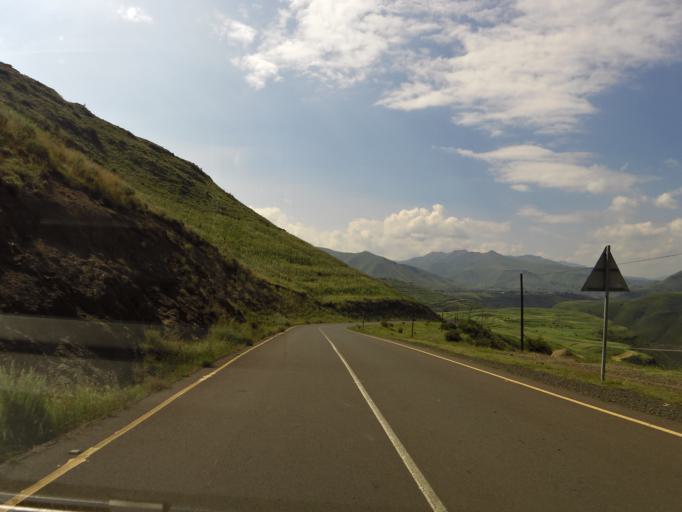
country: LS
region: Thaba-Tseka
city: Thaba-Tseka
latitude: -29.1378
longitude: 28.4941
